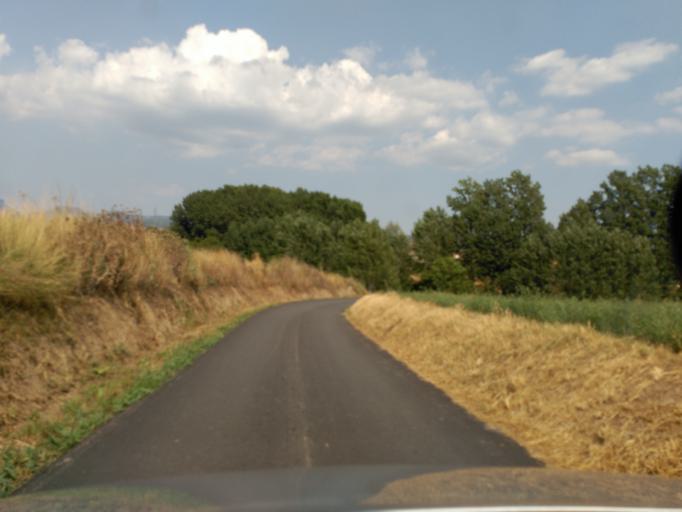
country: ES
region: Catalonia
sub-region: Provincia de Barcelona
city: Manlleu
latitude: 41.9895
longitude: 2.3021
